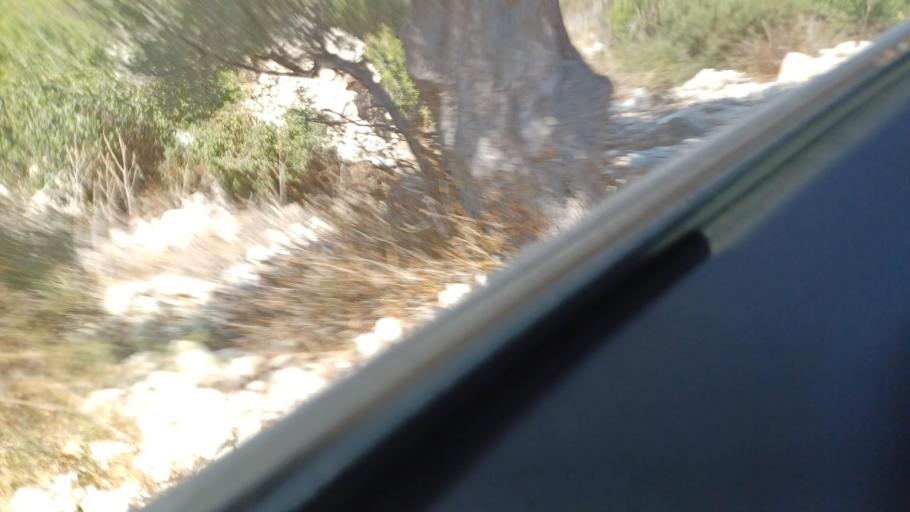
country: CY
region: Pafos
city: Tala
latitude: 34.8699
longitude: 32.4313
